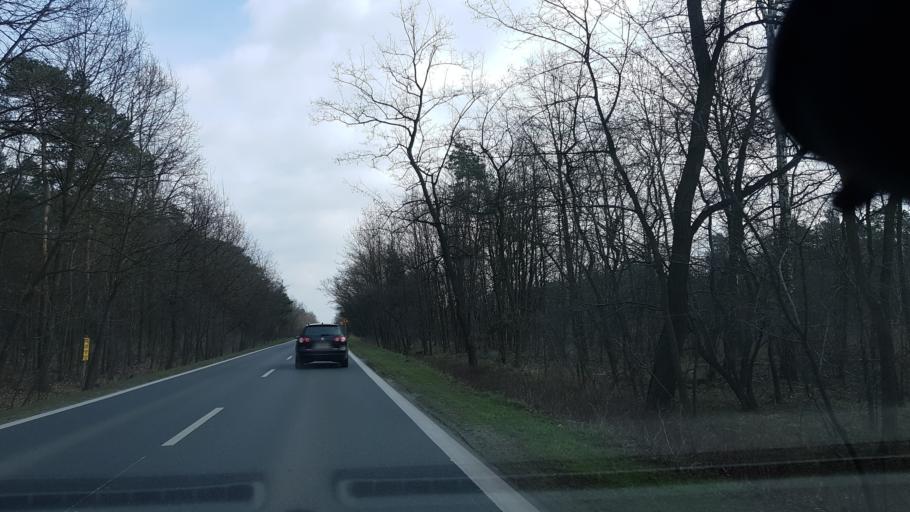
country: PL
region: Masovian Voivodeship
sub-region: Warszawa
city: Wesola
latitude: 52.2555
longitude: 21.2039
